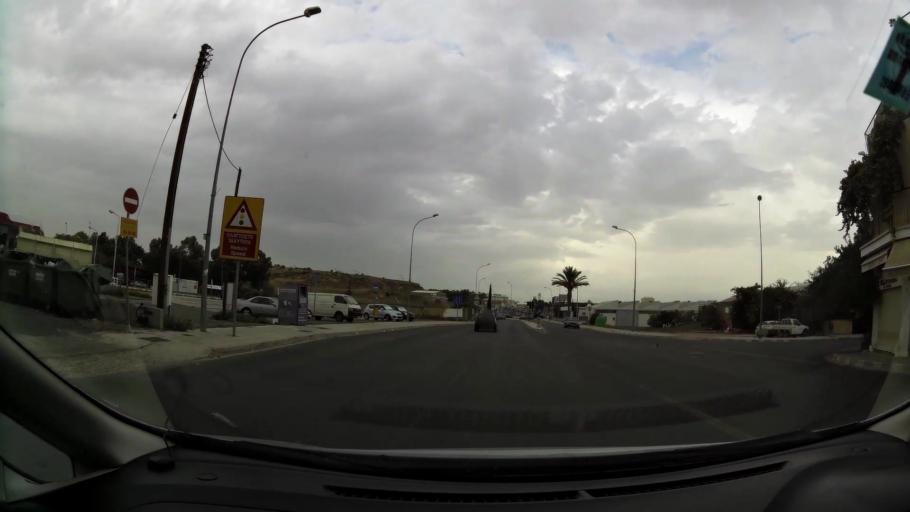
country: CY
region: Lefkosia
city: Geri
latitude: 35.1169
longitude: 33.3783
